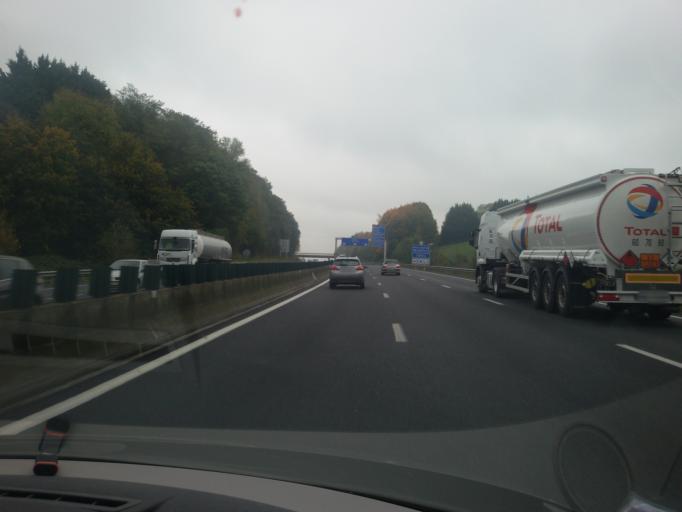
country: FR
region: Haute-Normandie
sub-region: Departement de l'Eure
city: Beuzeville
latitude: 49.3073
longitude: 0.2987
